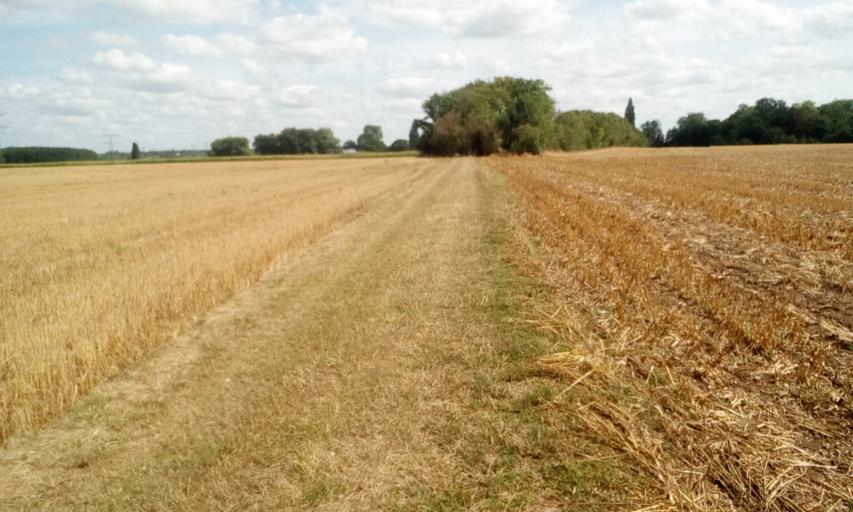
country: FR
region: Lower Normandy
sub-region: Departement du Calvados
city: Bellengreville
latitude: 49.1311
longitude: -0.2017
